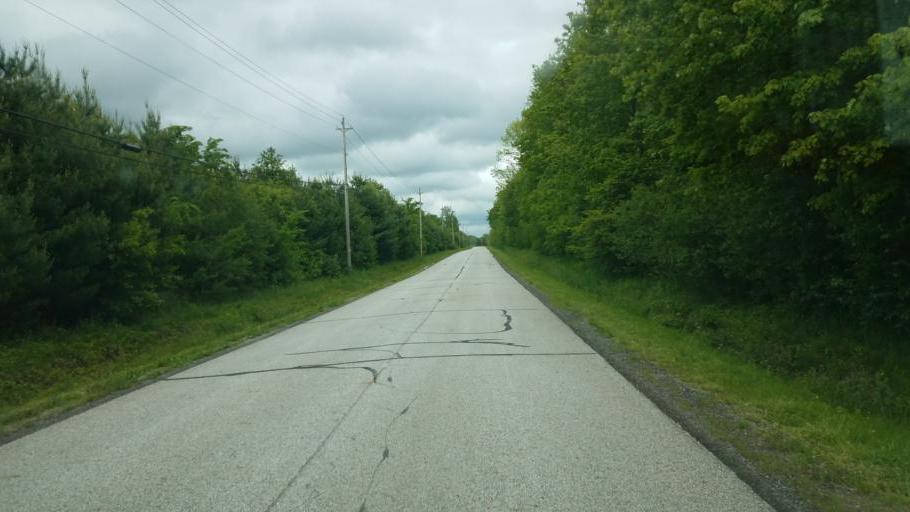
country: US
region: Ohio
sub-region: Geauga County
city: Burton
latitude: 41.4138
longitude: -81.1824
